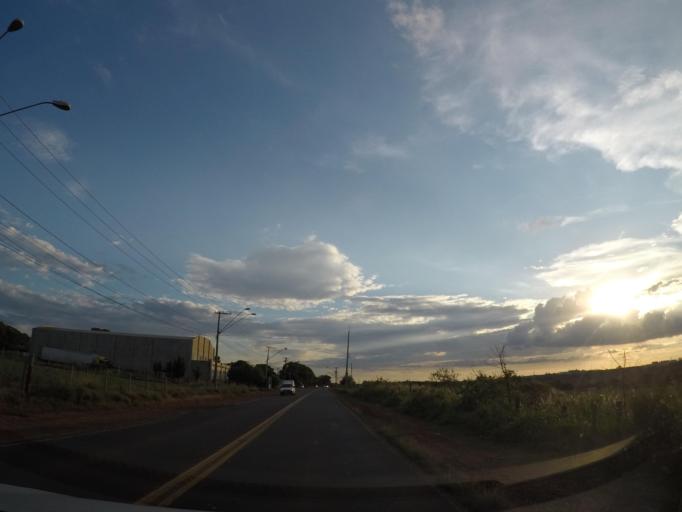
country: BR
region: Sao Paulo
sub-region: Sumare
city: Sumare
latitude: -22.8420
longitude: -47.2782
